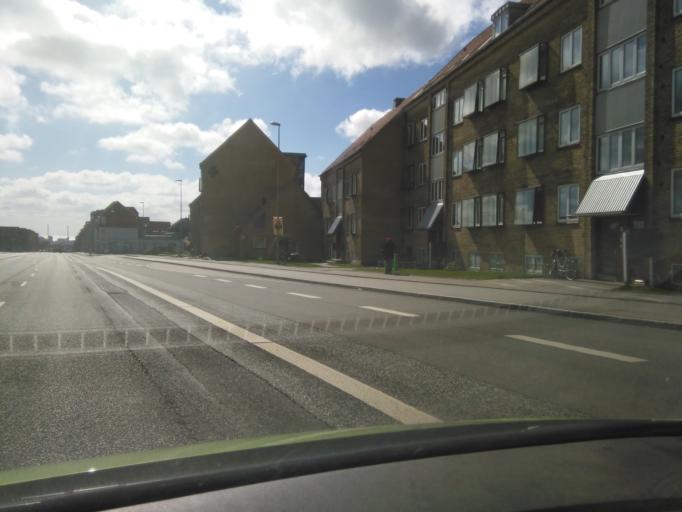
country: DK
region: Central Jutland
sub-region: Arhus Kommune
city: Arhus
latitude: 56.1779
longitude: 10.2004
